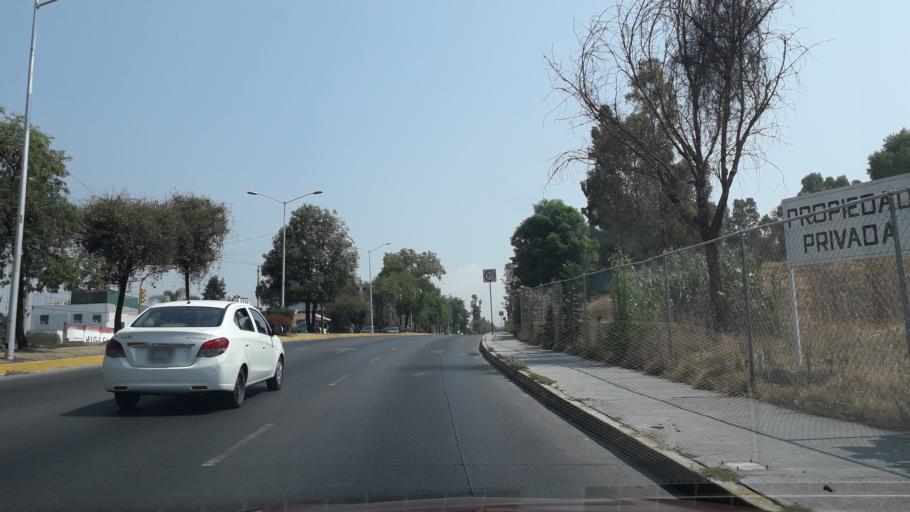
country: MX
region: Puebla
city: Puebla
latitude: 19.0560
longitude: -98.1897
